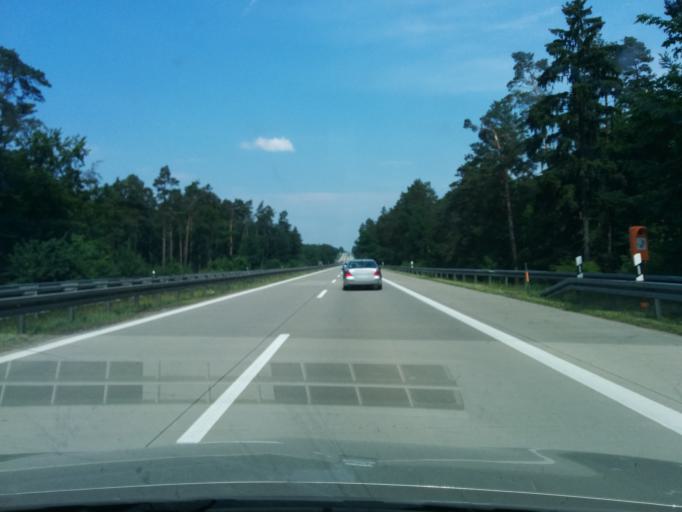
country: DE
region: Brandenburg
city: Althuttendorf
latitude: 53.0636
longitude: 13.8408
